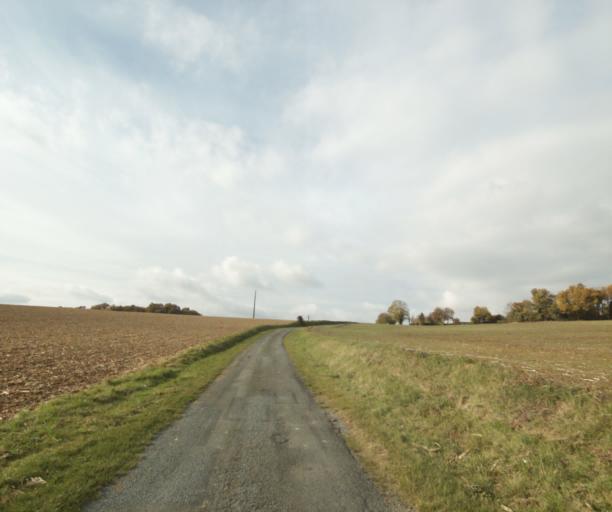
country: FR
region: Poitou-Charentes
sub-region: Departement de la Charente-Maritime
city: Saint-Georges-des-Coteaux
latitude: 45.7643
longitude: -0.6830
